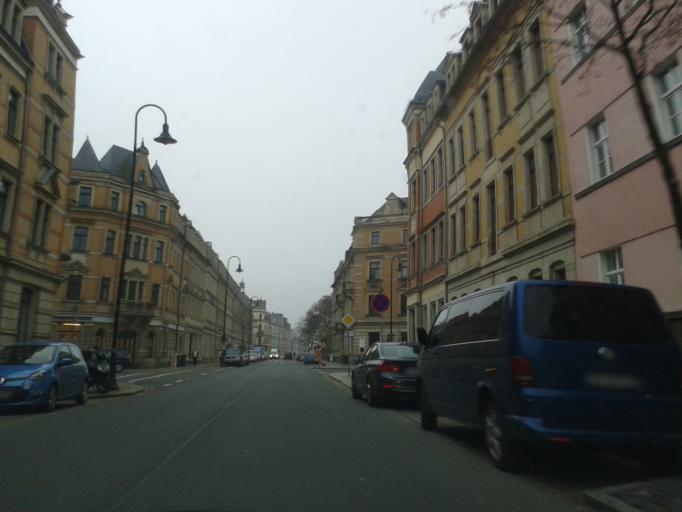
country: DE
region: Saxony
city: Dresden
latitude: 51.0792
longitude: 13.7198
